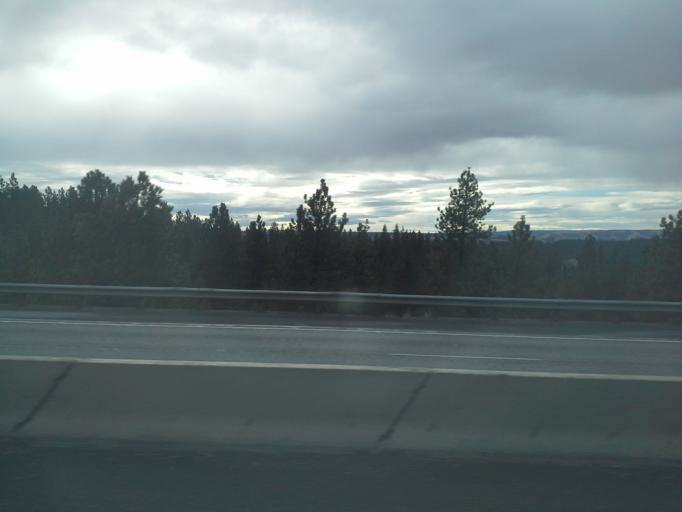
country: US
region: Oregon
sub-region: Umatilla County
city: Mission
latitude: 45.5882
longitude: -118.5617
